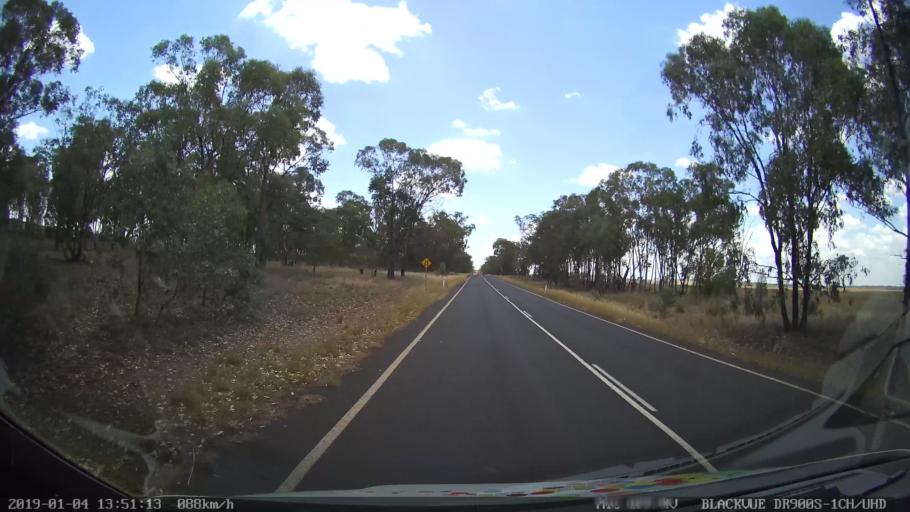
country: AU
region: New South Wales
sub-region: Dubbo Municipality
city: Dubbo
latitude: -32.4099
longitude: 148.5709
